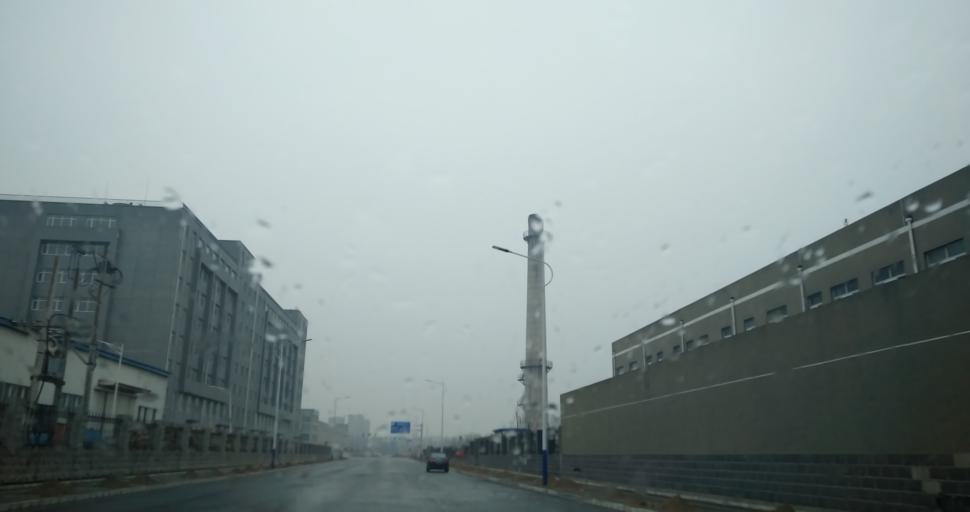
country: CN
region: Beijing
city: Yinghai
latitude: 39.7110
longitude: 116.4104
